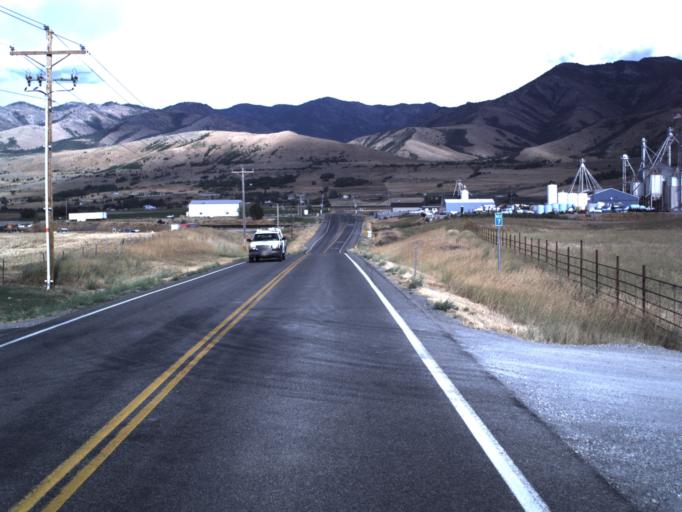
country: US
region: Utah
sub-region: Cache County
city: Lewiston
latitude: 41.9761
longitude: -111.8189
